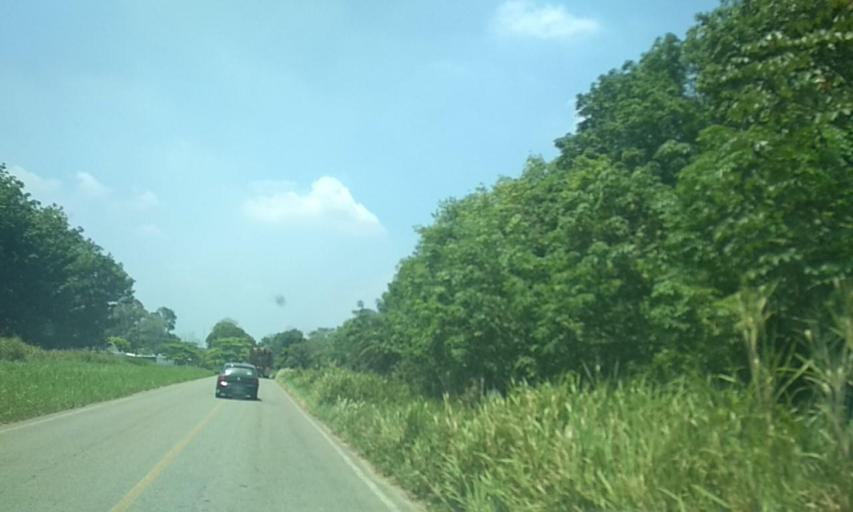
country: MX
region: Tabasco
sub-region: Huimanguillo
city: Paso de la Mina 3ra. Seccion
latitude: 17.8171
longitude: -93.6157
